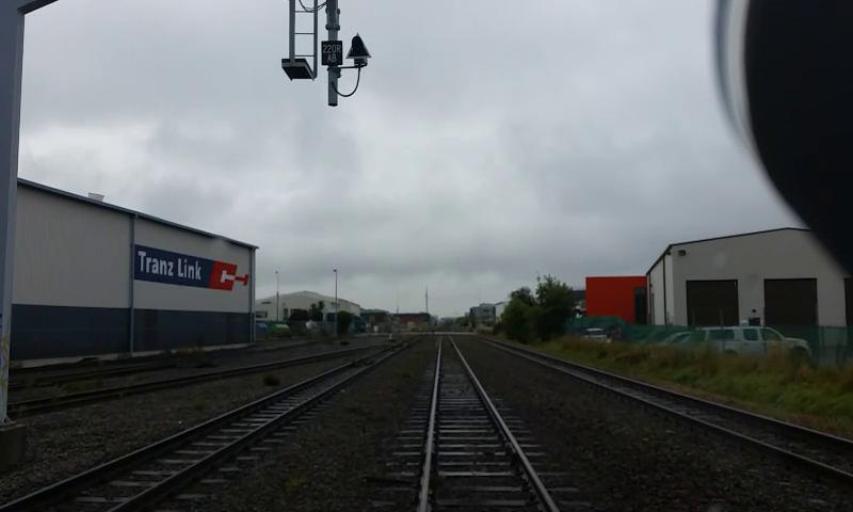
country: NZ
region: Canterbury
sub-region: Christchurch City
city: Christchurch
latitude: -43.5410
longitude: 172.5958
